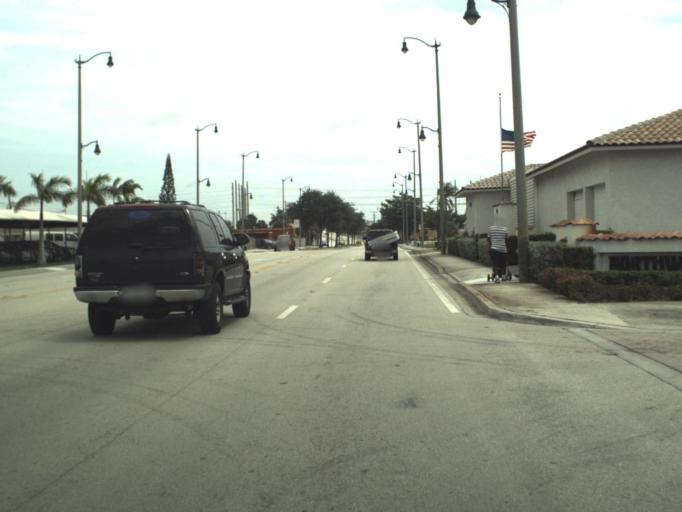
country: US
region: Florida
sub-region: Palm Beach County
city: Riviera Beach
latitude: 26.7602
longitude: -80.0554
